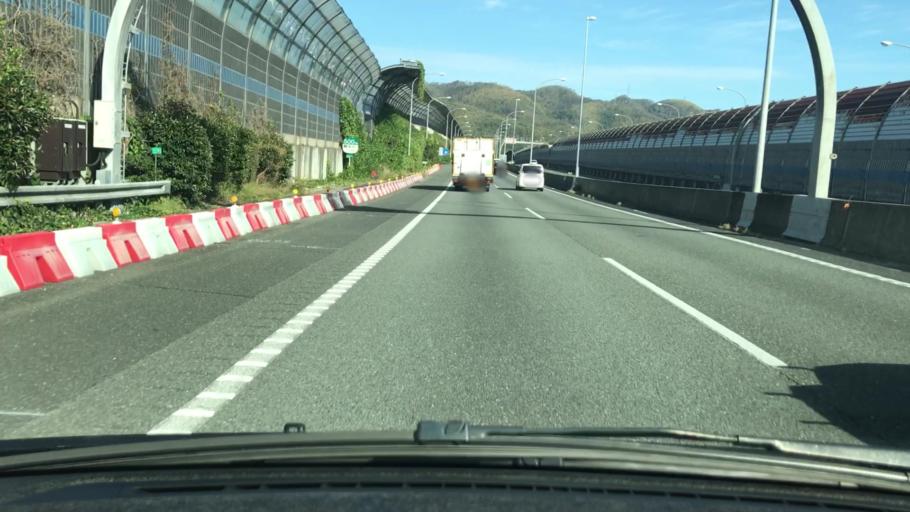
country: JP
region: Kyoto
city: Yawata
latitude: 34.8804
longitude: 135.6578
